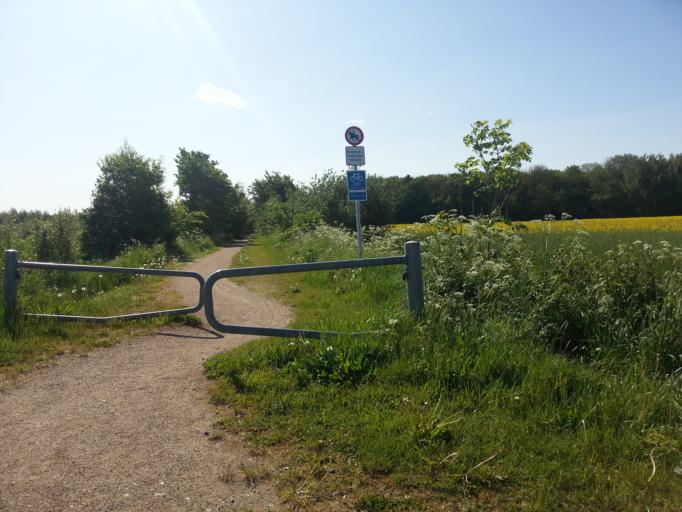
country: DK
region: North Denmark
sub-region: Alborg Kommune
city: Vadum
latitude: 57.1178
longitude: 9.8704
